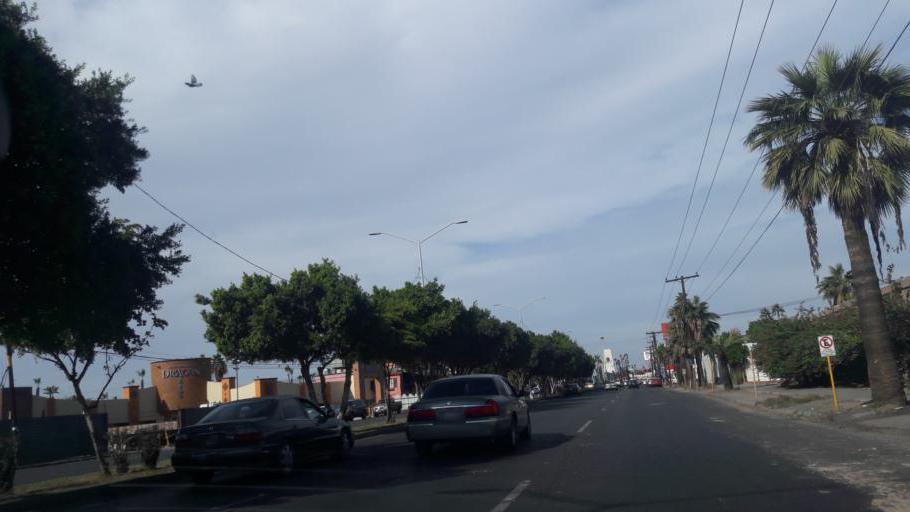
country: MX
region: Baja California
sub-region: Mexicali
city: Mexicali
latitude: 32.6445
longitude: -115.4511
